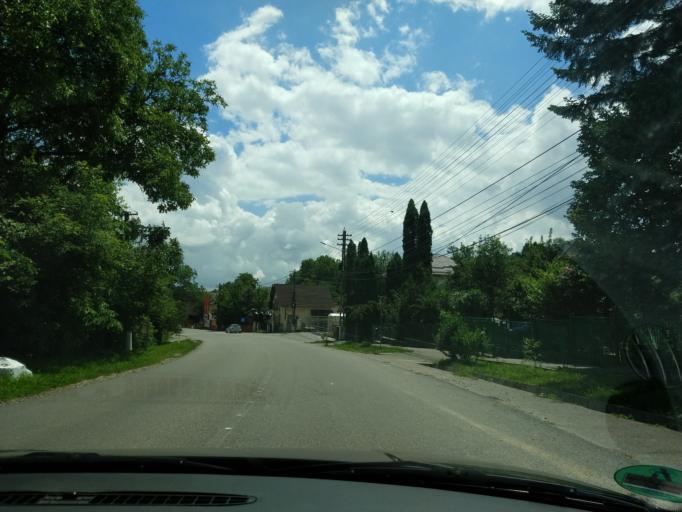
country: RO
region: Prahova
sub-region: Comuna Cornu
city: Cornu de Jos
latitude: 45.1503
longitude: 25.6886
